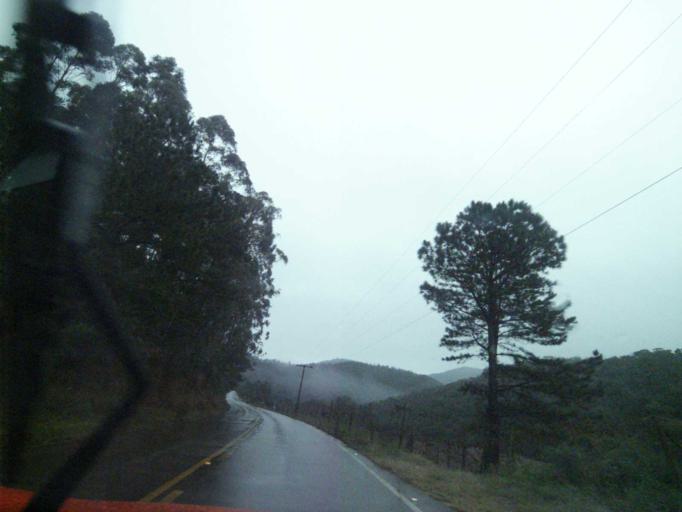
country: BR
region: Santa Catarina
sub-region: Anitapolis
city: Anitapolis
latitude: -27.8444
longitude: -49.0530
